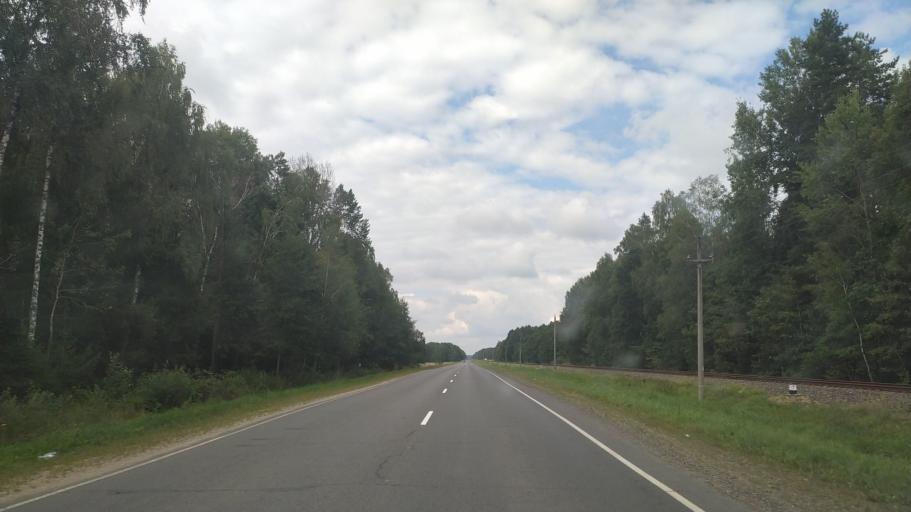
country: BY
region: Brest
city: Byelaazyorsk
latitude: 52.5343
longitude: 25.1419
